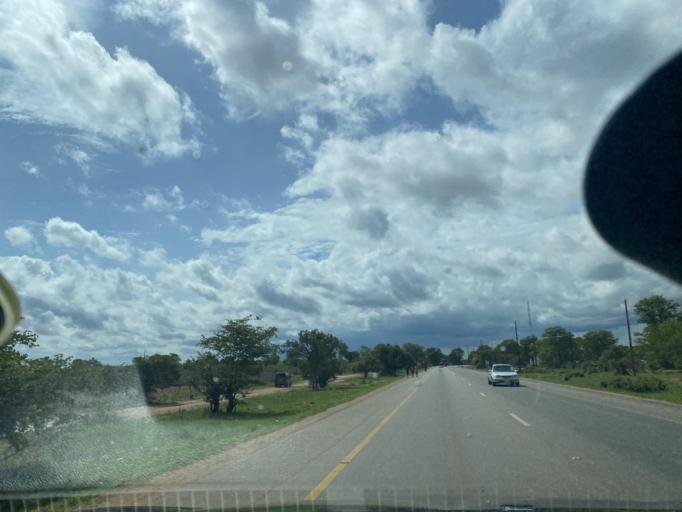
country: ZM
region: Lusaka
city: Kafue
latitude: -15.8545
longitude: 28.2549
